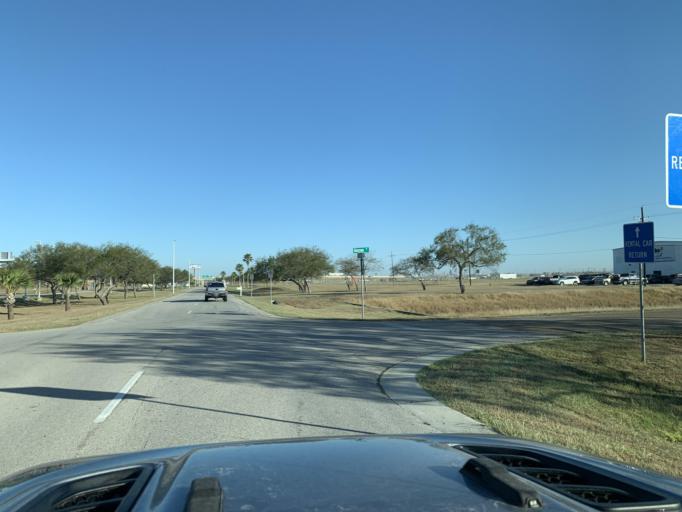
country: US
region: Texas
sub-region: Nueces County
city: Corpus Christi
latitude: 27.7800
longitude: -97.5020
